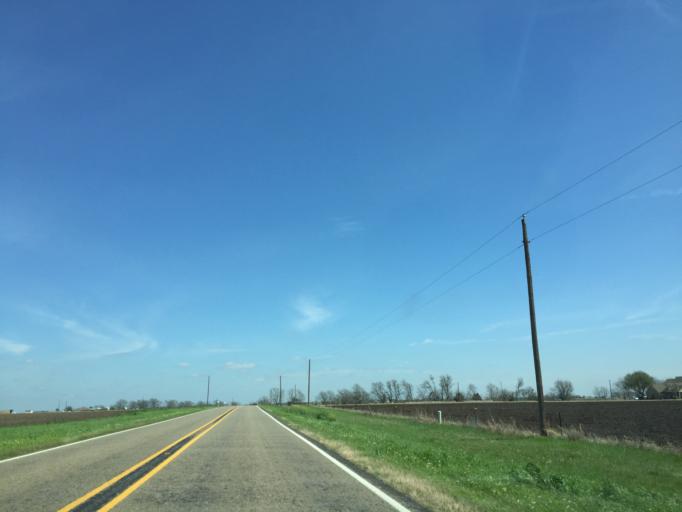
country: US
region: Texas
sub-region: Williamson County
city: Taylor
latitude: 30.5675
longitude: -97.3444
